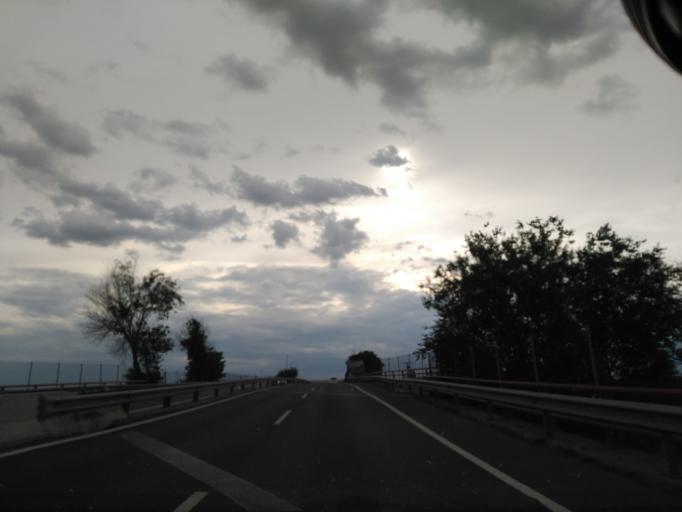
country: ES
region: Madrid
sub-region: Provincia de Madrid
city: Torrejon de Ardoz
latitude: 40.4682
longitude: -3.4282
